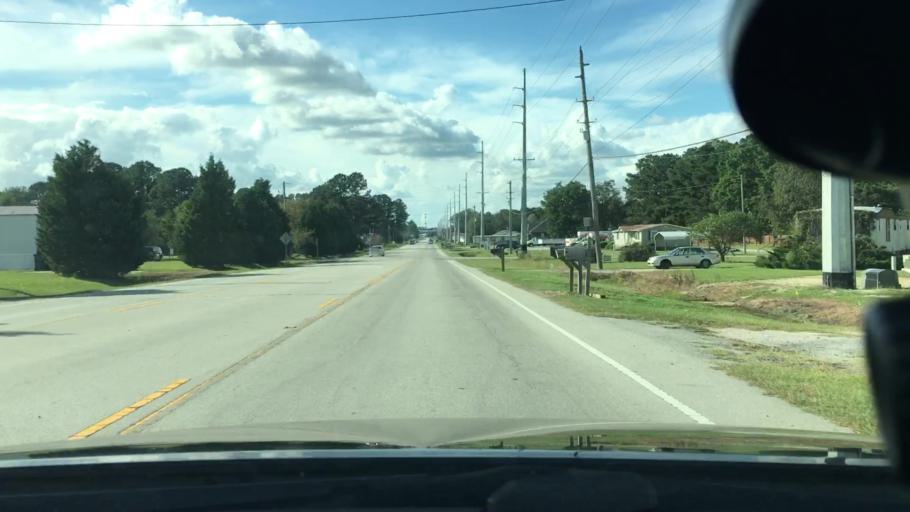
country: US
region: North Carolina
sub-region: Pitt County
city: Windsor
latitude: 35.5559
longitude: -77.3317
